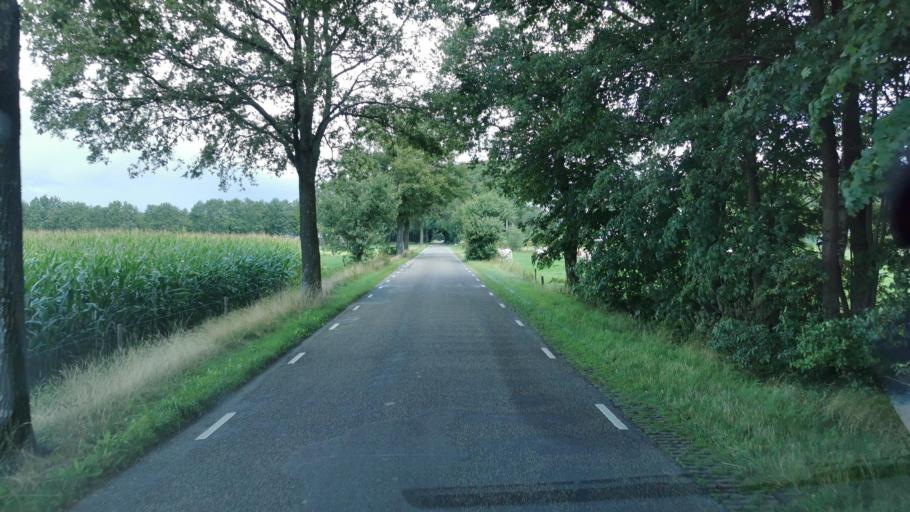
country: NL
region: Overijssel
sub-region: Gemeente Losser
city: Losser
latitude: 52.2739
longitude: 7.0178
